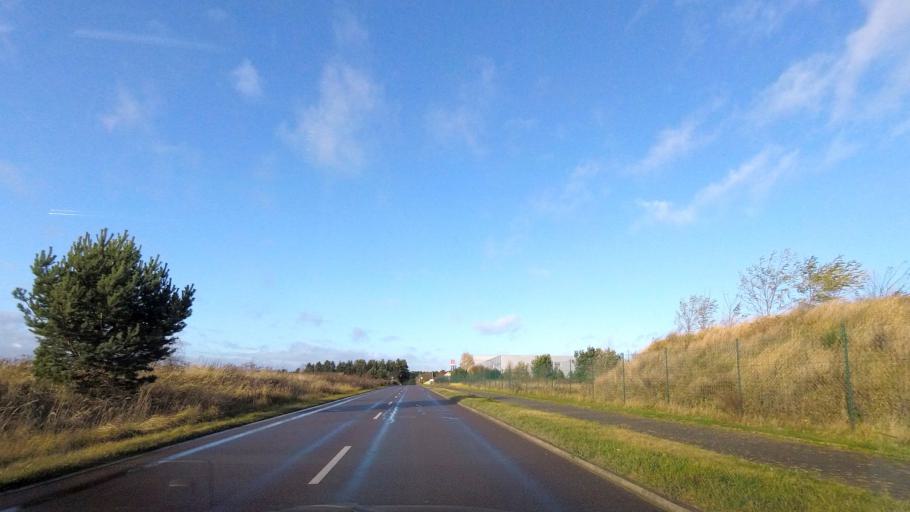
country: DE
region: Brandenburg
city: Niemegk
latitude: 52.0867
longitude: 12.7045
